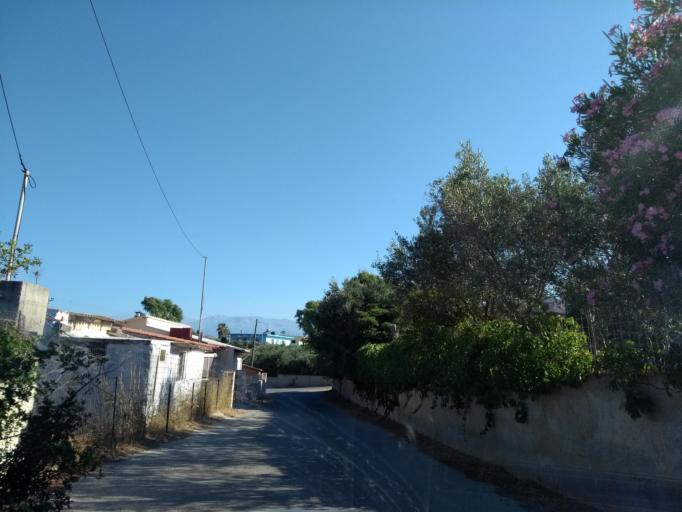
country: GR
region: Crete
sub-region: Nomos Chanias
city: Pithari
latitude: 35.5876
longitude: 24.0919
